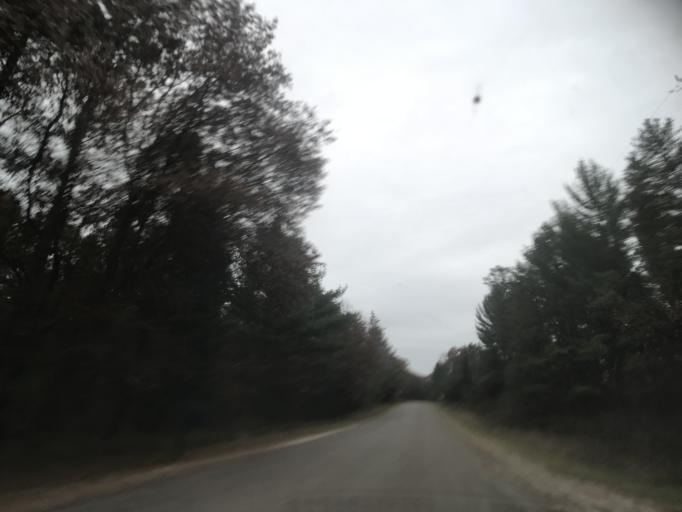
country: US
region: Wisconsin
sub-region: Oconto County
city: Gillett
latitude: 45.2705
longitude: -88.2561
